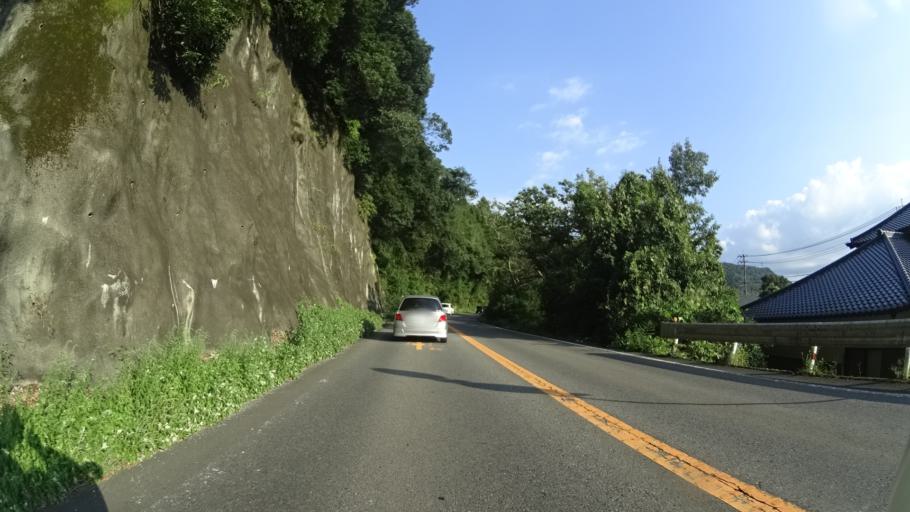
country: JP
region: Oita
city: Bungo-Takada-shi
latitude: 33.4491
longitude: 131.3312
